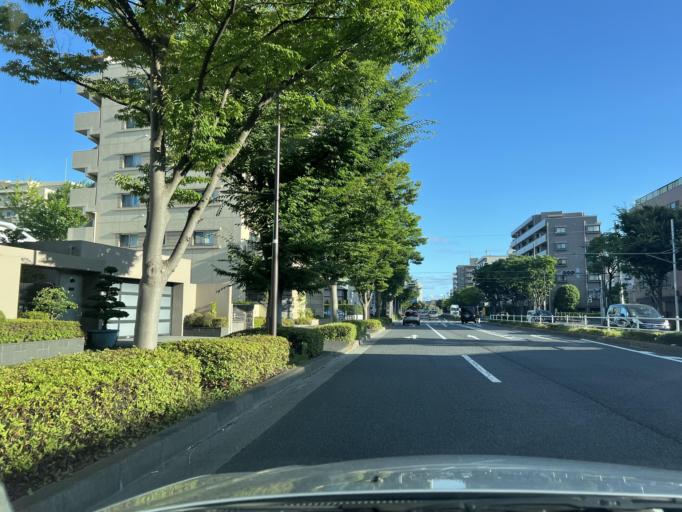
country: JP
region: Tokyo
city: Urayasu
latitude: 35.6622
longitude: 139.8817
